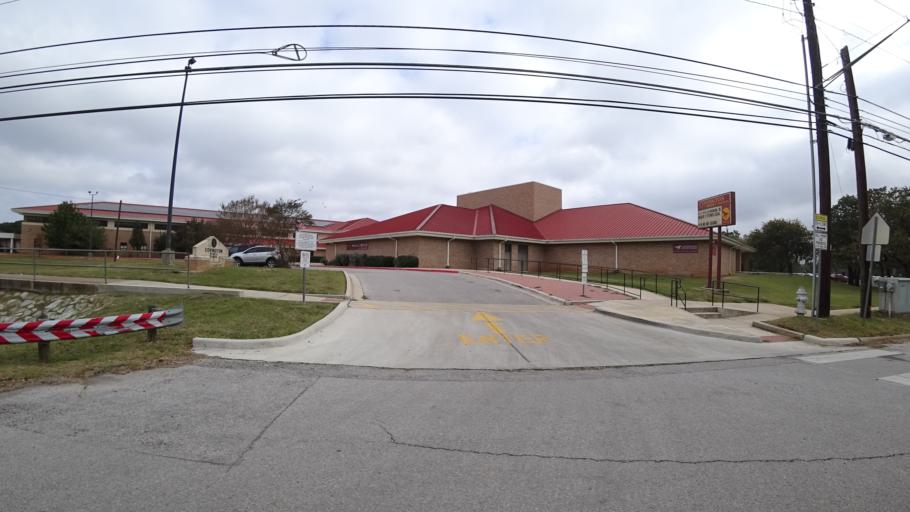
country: US
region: Texas
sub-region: Travis County
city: Shady Hollow
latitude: 30.2116
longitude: -97.8349
